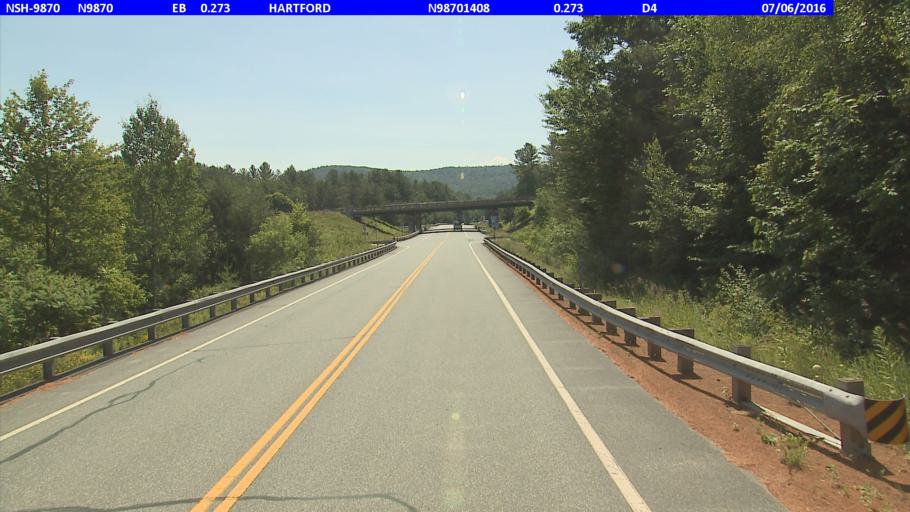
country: US
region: Vermont
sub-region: Windsor County
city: Wilder
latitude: 43.6671
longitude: -72.3209
